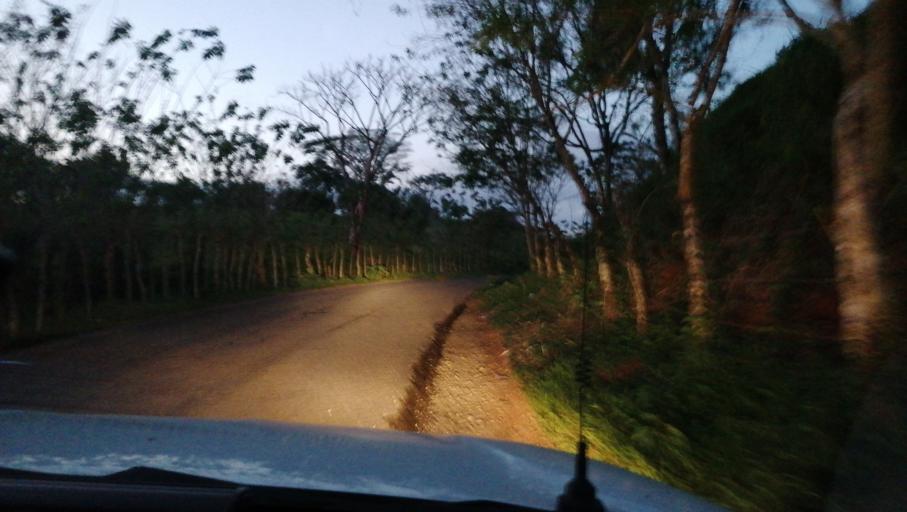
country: MX
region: Chiapas
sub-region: Ostuacan
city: Nuevo Juan del Grijalva
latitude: 17.4716
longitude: -93.3472
